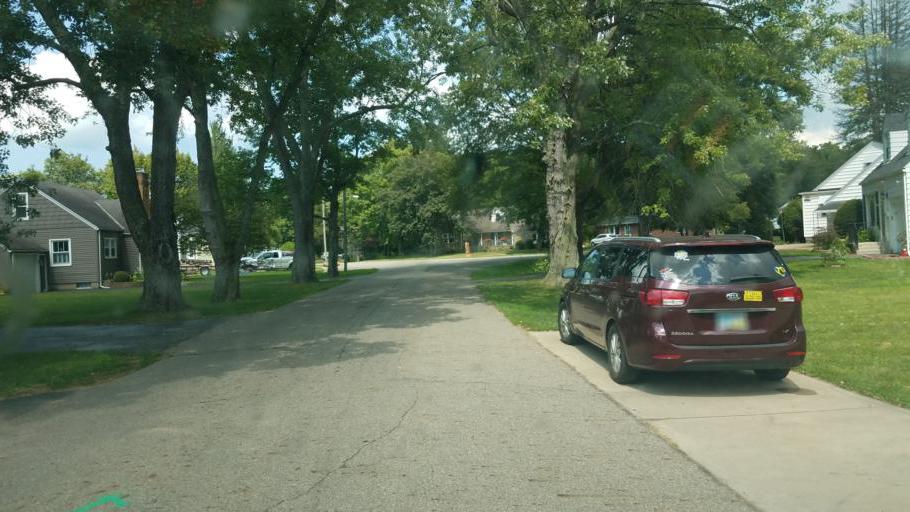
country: US
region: Ohio
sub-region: Knox County
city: Mount Vernon
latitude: 40.3961
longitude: -82.4657
